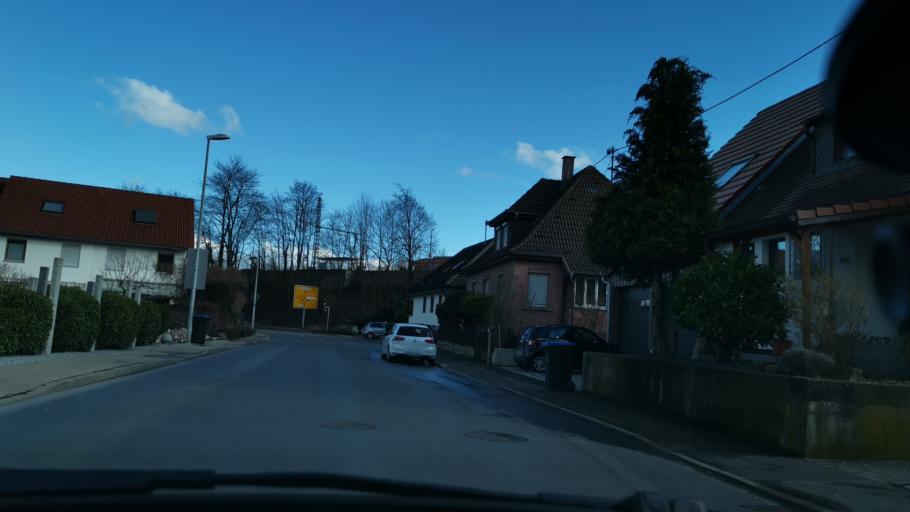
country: DE
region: Baden-Wuerttemberg
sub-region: Regierungsbezirk Stuttgart
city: Renningen
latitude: 48.7724
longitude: 8.9049
